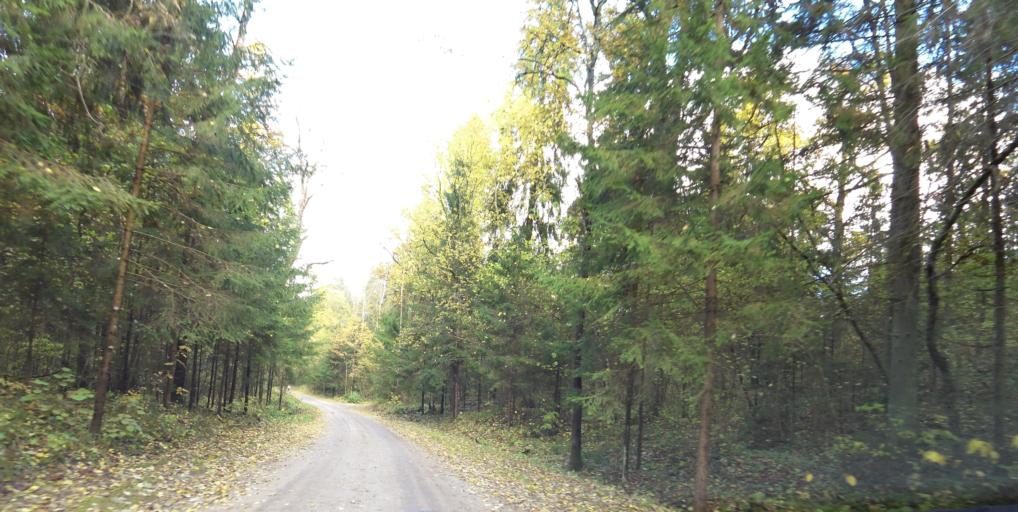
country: LT
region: Vilnius County
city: Vilkpede
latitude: 54.6525
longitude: 25.2558
